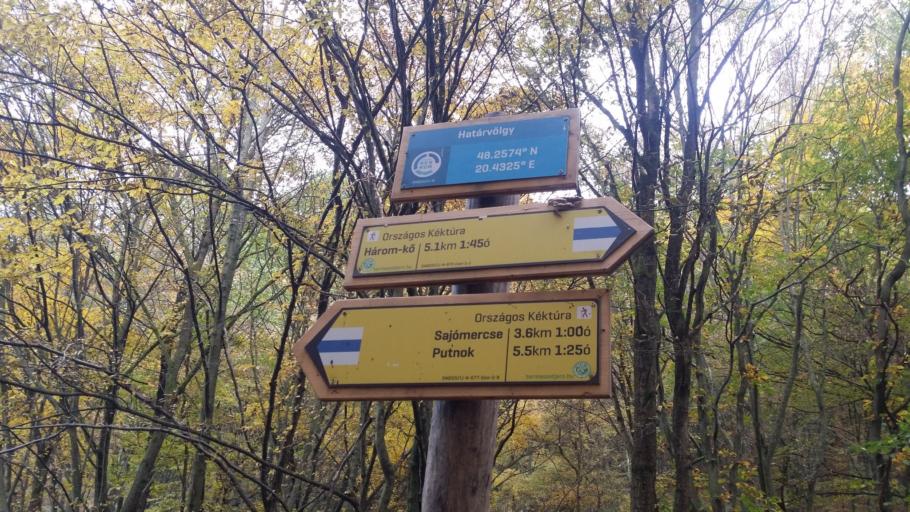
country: HU
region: Borsod-Abauj-Zemplen
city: Putnok
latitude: 48.2568
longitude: 20.4326
